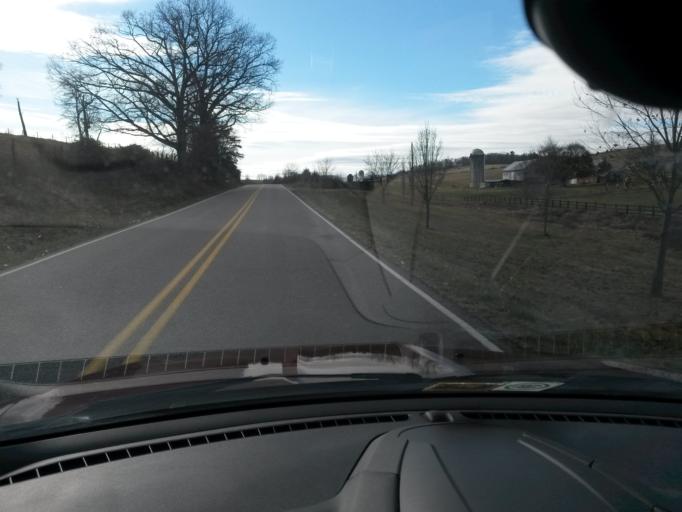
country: US
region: Virginia
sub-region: Rockingham County
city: Bridgewater
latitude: 38.3300
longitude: -79.0536
